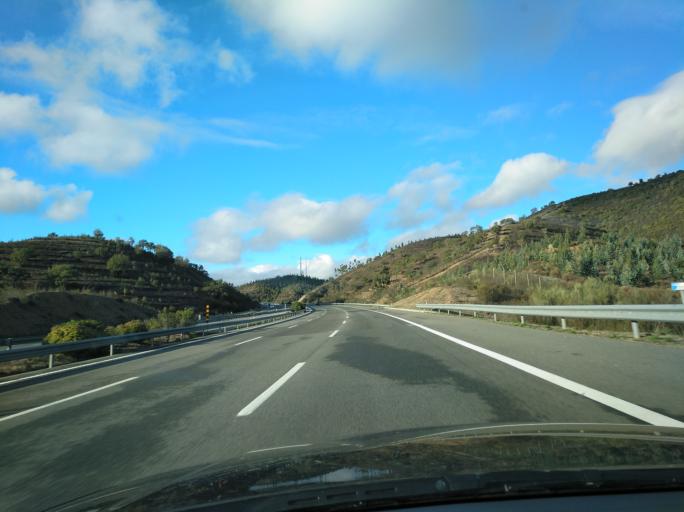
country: PT
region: Faro
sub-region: Silves
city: Sao Bartolomeu de Messines
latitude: 37.3950
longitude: -8.2602
